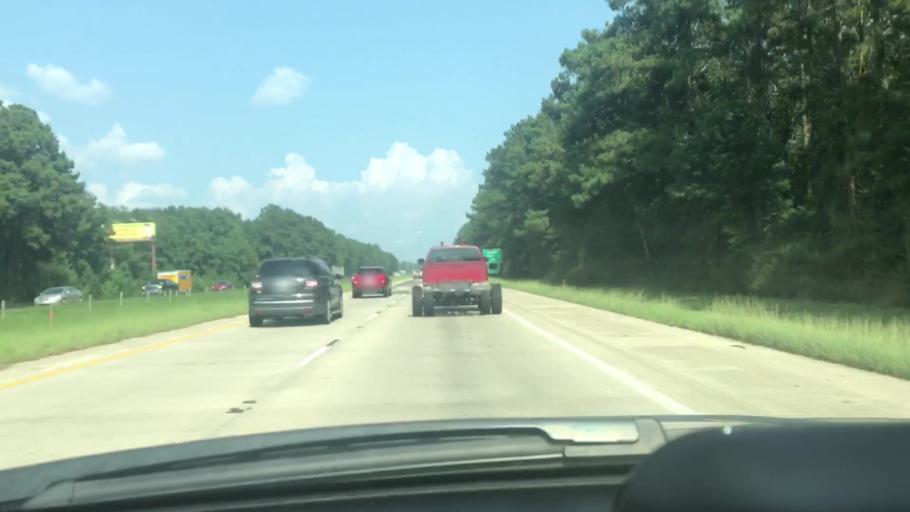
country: US
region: Louisiana
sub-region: Livingston Parish
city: Albany
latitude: 30.4792
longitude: -90.5331
